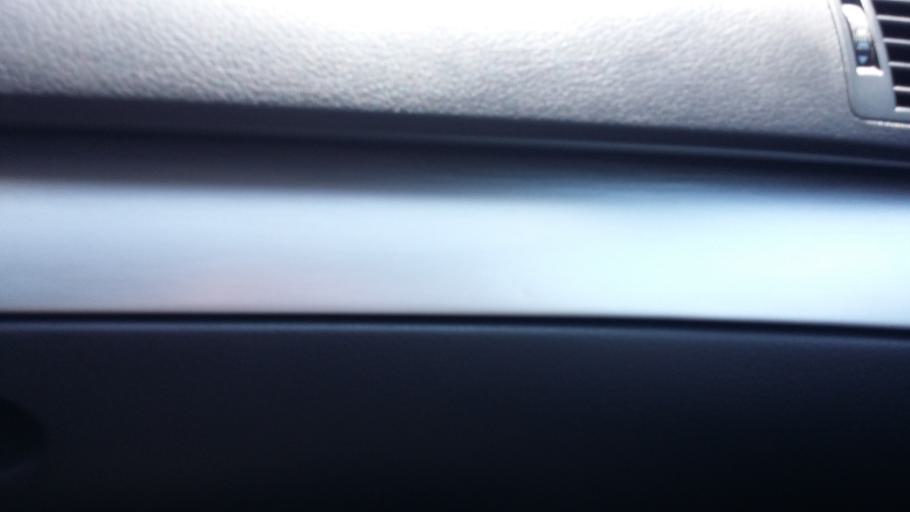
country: MX
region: Baja California
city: Ensenada
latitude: 31.8146
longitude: -116.5977
